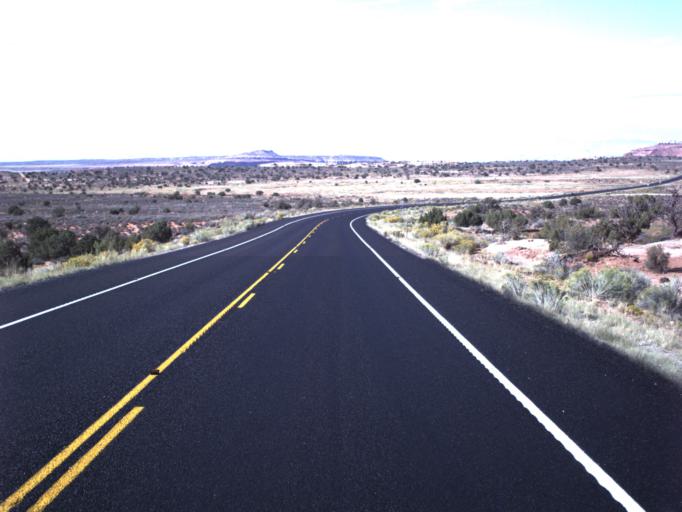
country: US
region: Utah
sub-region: Grand County
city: Moab
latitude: 38.6086
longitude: -109.8172
